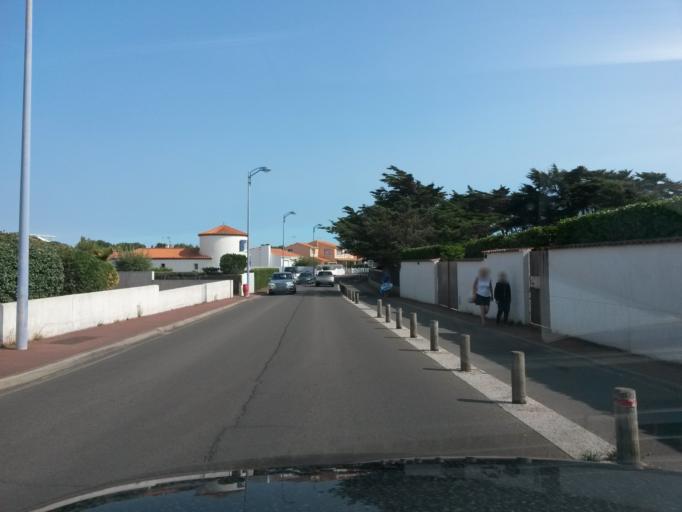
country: FR
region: Pays de la Loire
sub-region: Departement de la Vendee
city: Bretignolles-sur-Mer
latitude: 46.6289
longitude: -1.8759
